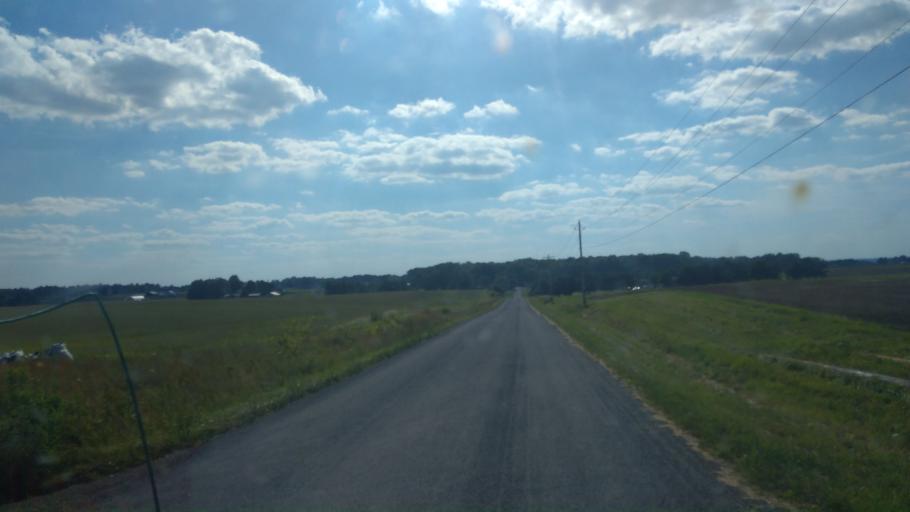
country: US
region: Ohio
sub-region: Wayne County
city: Apple Creek
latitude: 40.7184
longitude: -81.8965
